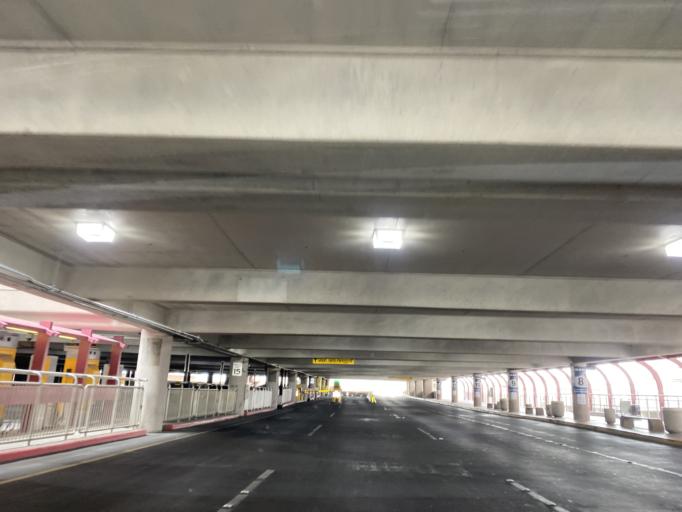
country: US
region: Nevada
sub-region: Clark County
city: Paradise
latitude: 36.0865
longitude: -115.1482
